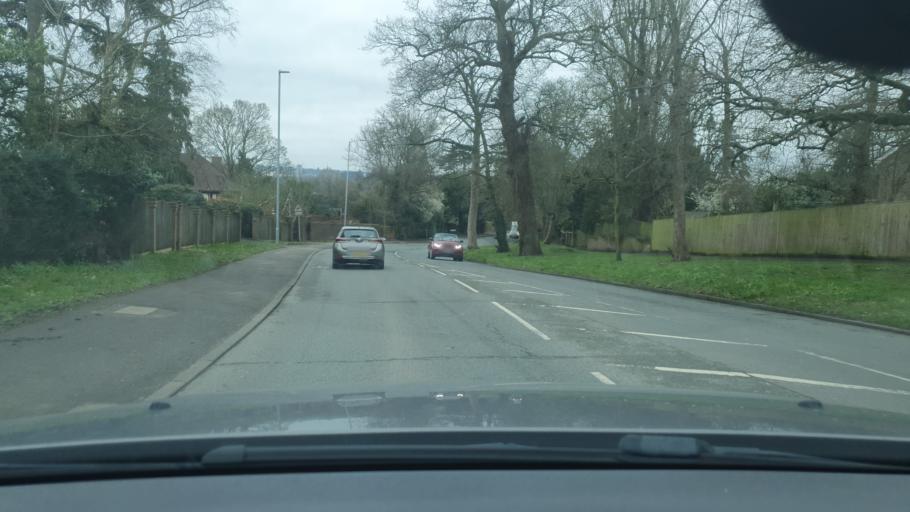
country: GB
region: England
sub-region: Reading
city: Reading
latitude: 51.4760
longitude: -0.9670
